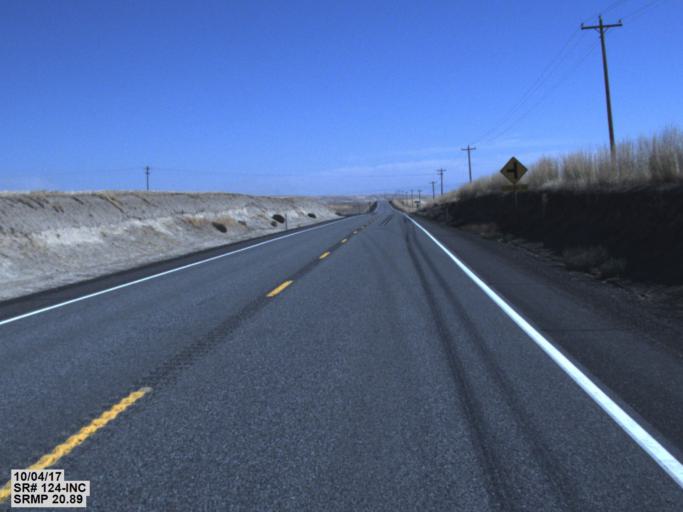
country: US
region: Washington
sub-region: Walla Walla County
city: Garrett
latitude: 46.2963
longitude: -118.6197
